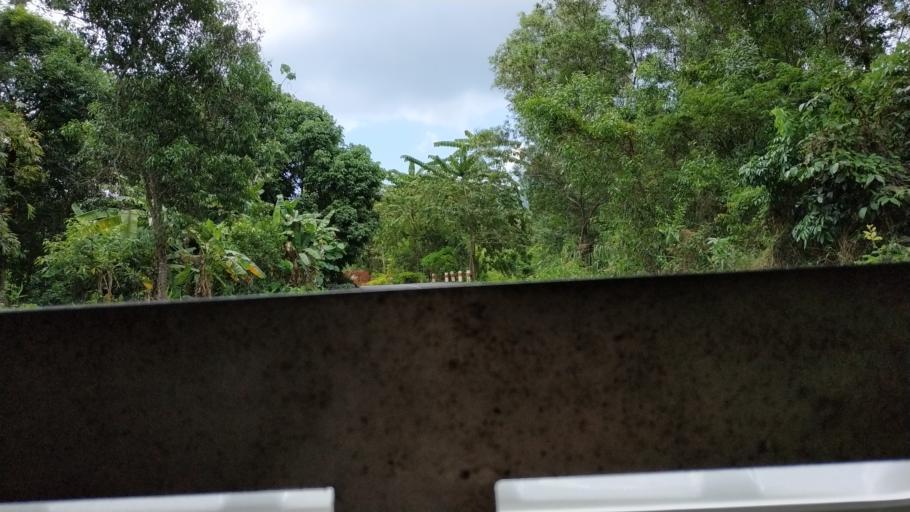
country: MM
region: Mon
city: Kyaikto
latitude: 17.4310
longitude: 97.0922
